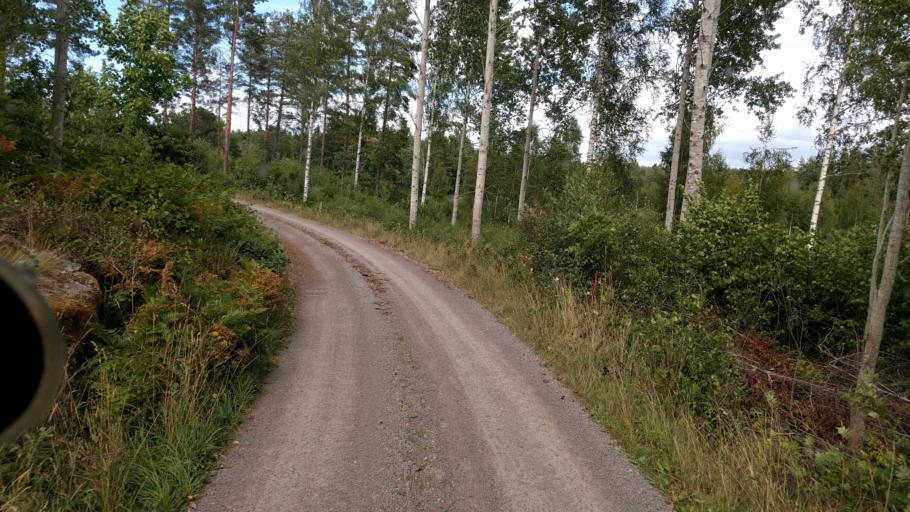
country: SE
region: Kalmar
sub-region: Vasterviks Kommun
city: Ankarsrum
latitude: 57.7279
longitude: 16.0947
